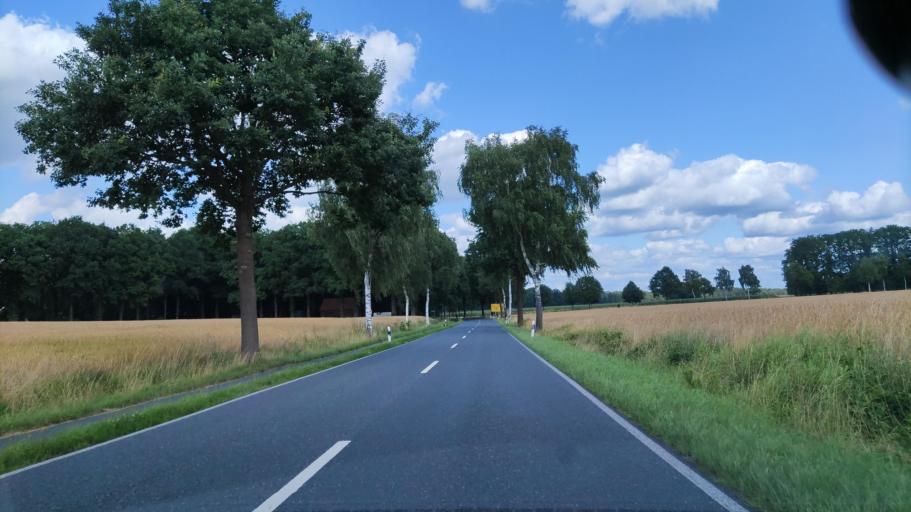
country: DE
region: Lower Saxony
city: Soltau
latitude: 52.9630
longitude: 9.7935
